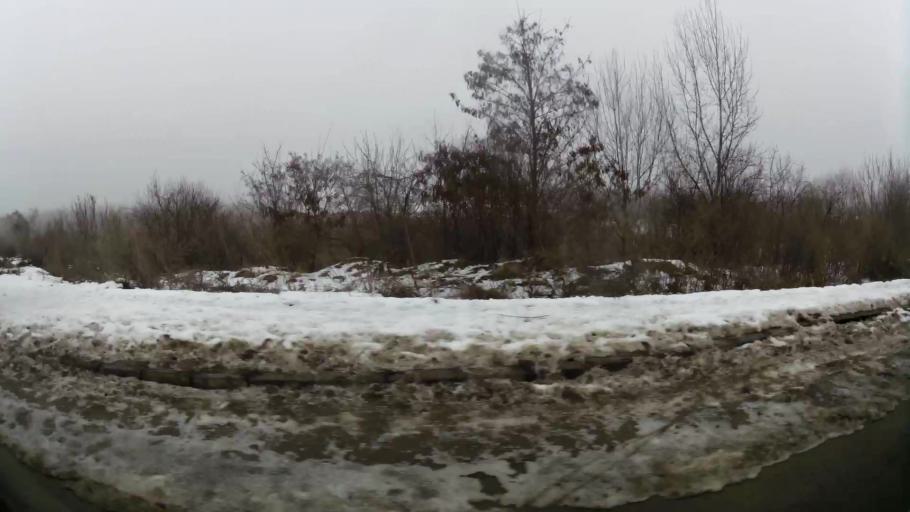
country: RO
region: Ilfov
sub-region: Comuna Chiajna
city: Rosu
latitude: 44.4586
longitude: 25.9948
